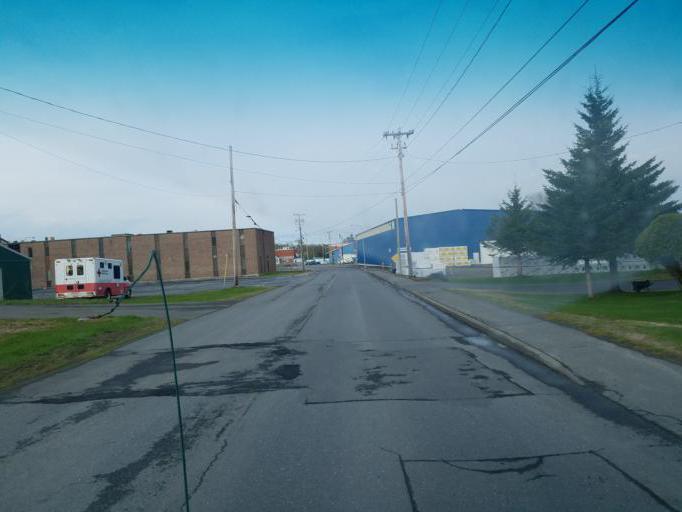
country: US
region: Maine
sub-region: Aroostook County
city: Caribou
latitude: 46.8588
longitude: -68.0171
